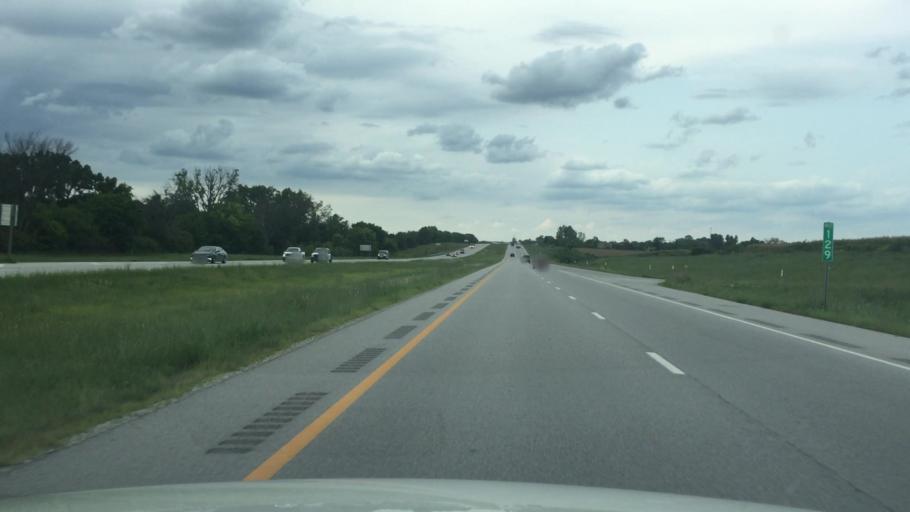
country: US
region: Kansas
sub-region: Miami County
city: Louisburg
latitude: 38.7248
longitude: -94.6761
